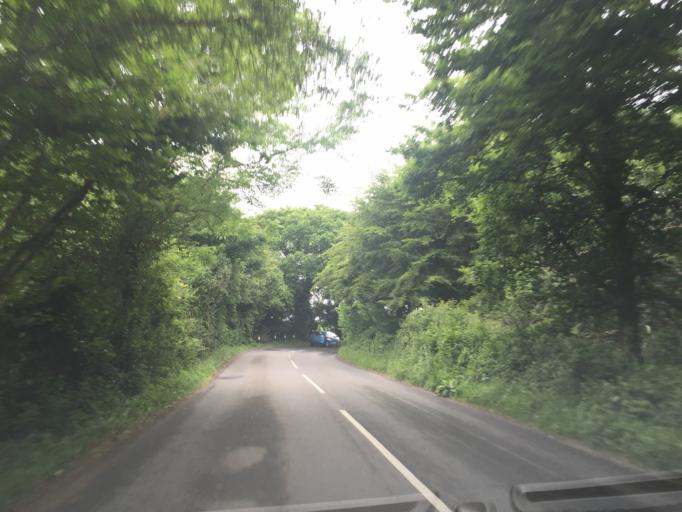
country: GB
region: England
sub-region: Dorset
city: Wareham
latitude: 50.6439
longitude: -2.0542
